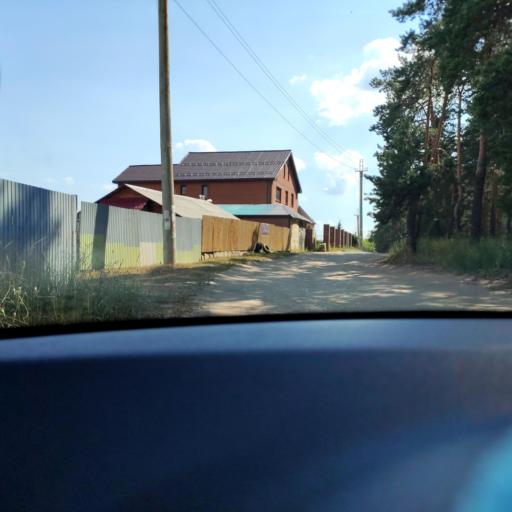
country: RU
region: Samara
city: Volzhskiy
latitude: 53.4408
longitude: 50.1686
